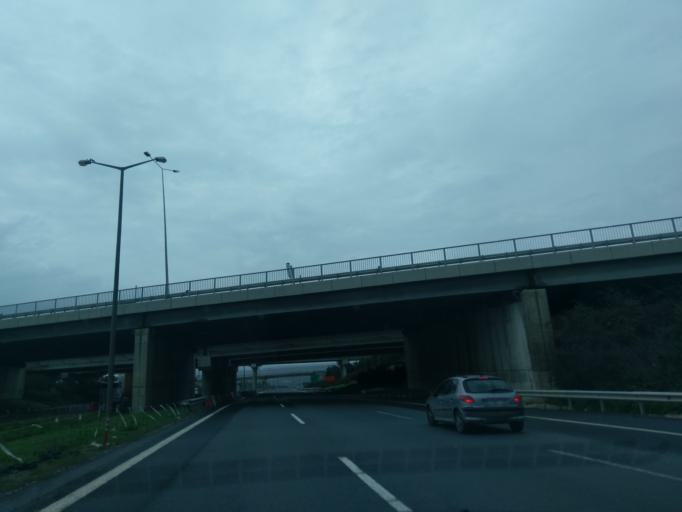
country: TR
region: Istanbul
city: Silivri
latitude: 41.1190
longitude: 28.1852
